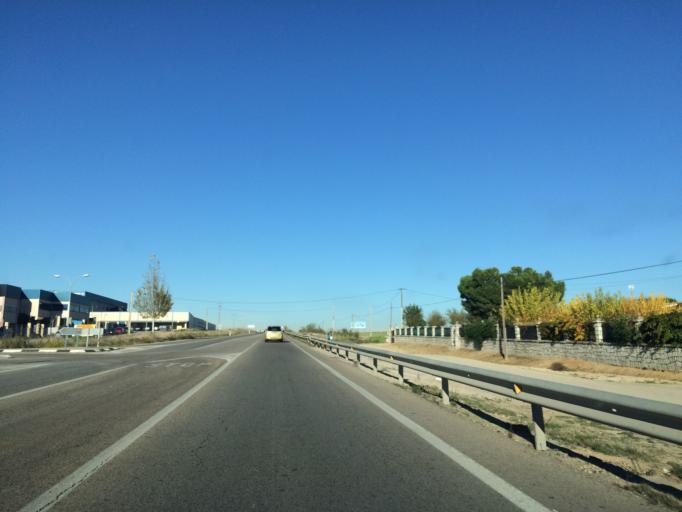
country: ES
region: Madrid
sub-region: Provincia de Madrid
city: Serranillos del Valle
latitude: 40.1957
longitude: -3.8738
